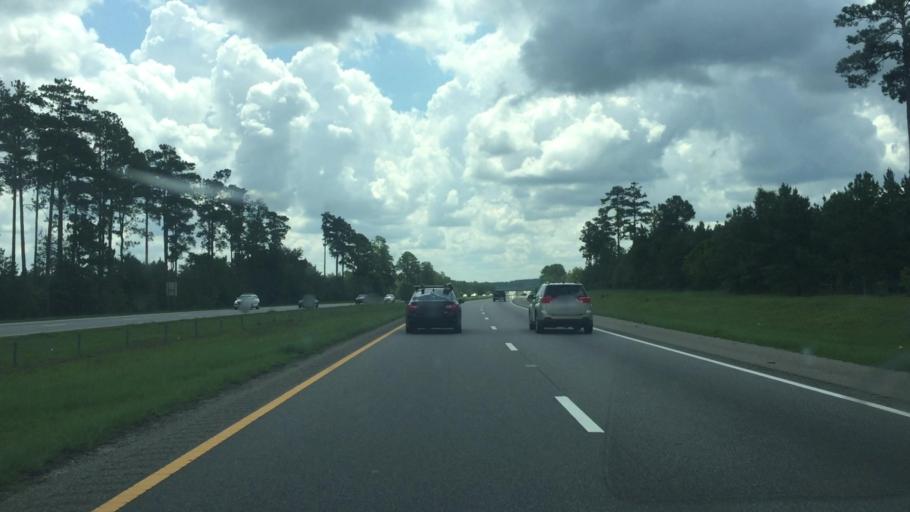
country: US
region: North Carolina
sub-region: Richmond County
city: East Rockingham
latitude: 34.8676
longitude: -79.7540
